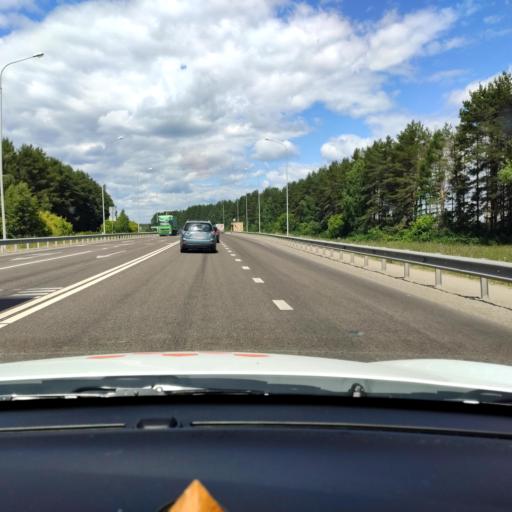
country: RU
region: Mariy-El
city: Pomary
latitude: 55.9207
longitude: 48.3729
